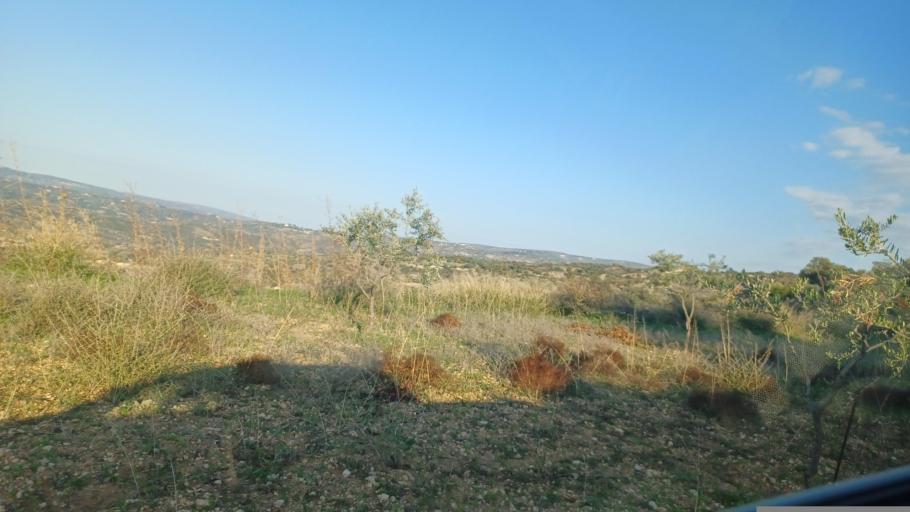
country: CY
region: Pafos
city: Mesogi
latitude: 34.8660
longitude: 32.5782
